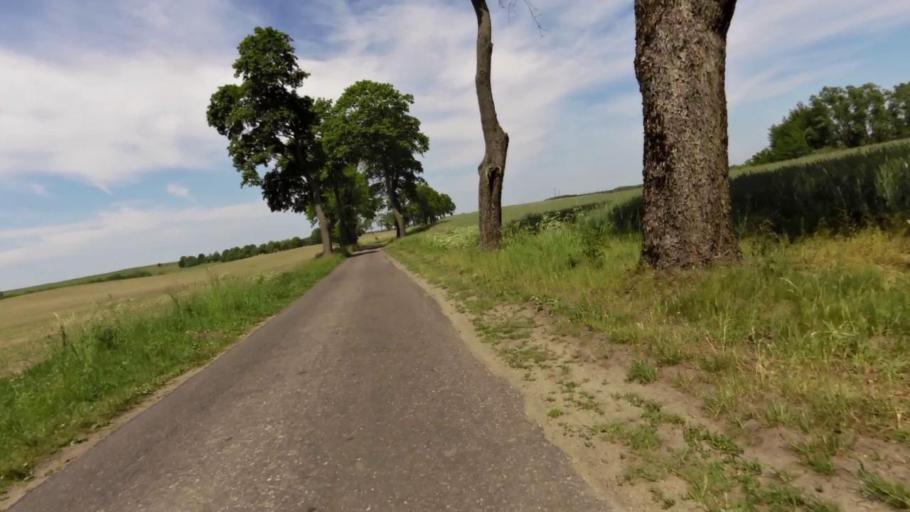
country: PL
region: West Pomeranian Voivodeship
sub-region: Powiat szczecinecki
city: Szczecinek
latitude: 53.6443
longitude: 16.6820
